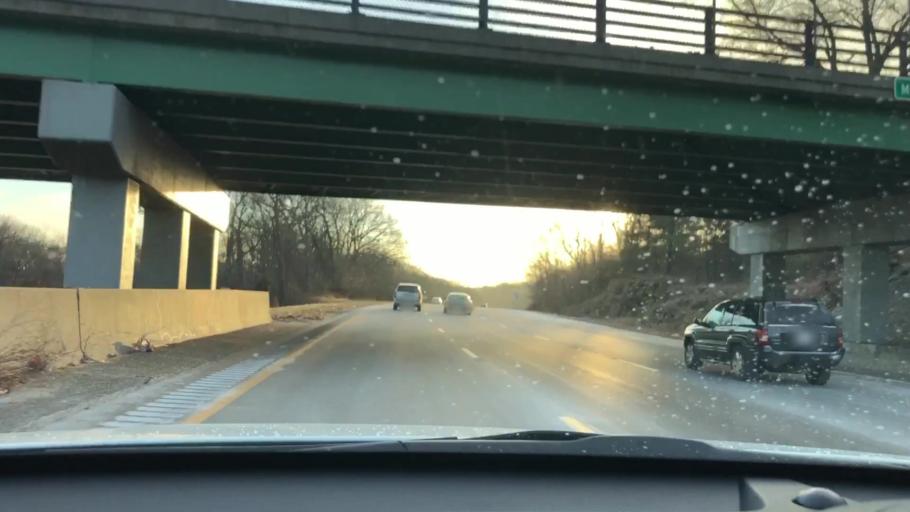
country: US
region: Massachusetts
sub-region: Norfolk County
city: Weymouth
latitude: 42.1929
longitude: -70.9502
